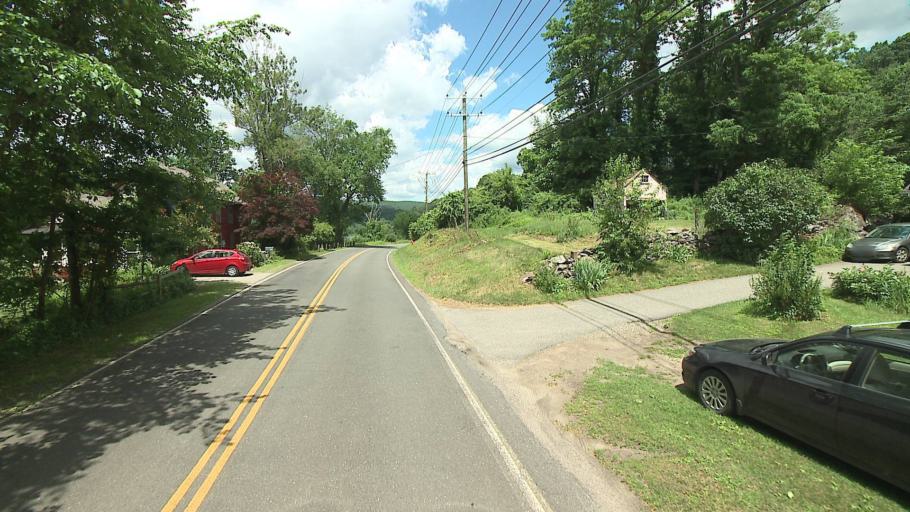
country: US
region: Connecticut
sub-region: Litchfield County
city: Kent
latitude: 41.6825
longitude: -73.4732
